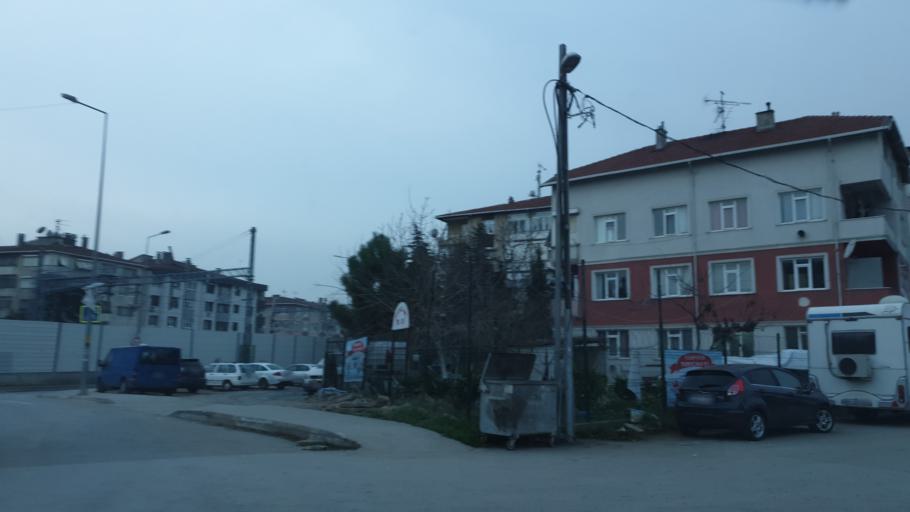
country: TR
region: Istanbul
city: Pendik
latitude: 40.8810
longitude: 29.2363
